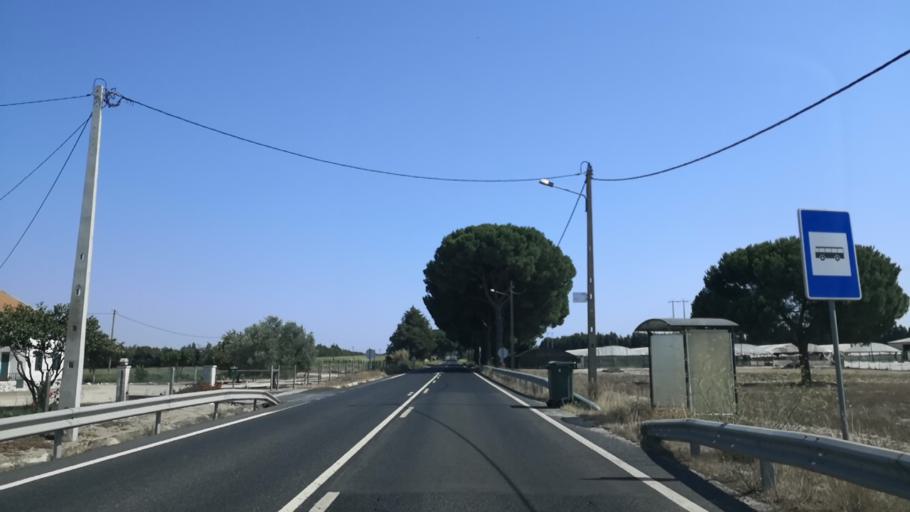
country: PT
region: Santarem
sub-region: Benavente
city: Poceirao
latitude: 38.7333
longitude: -8.6506
